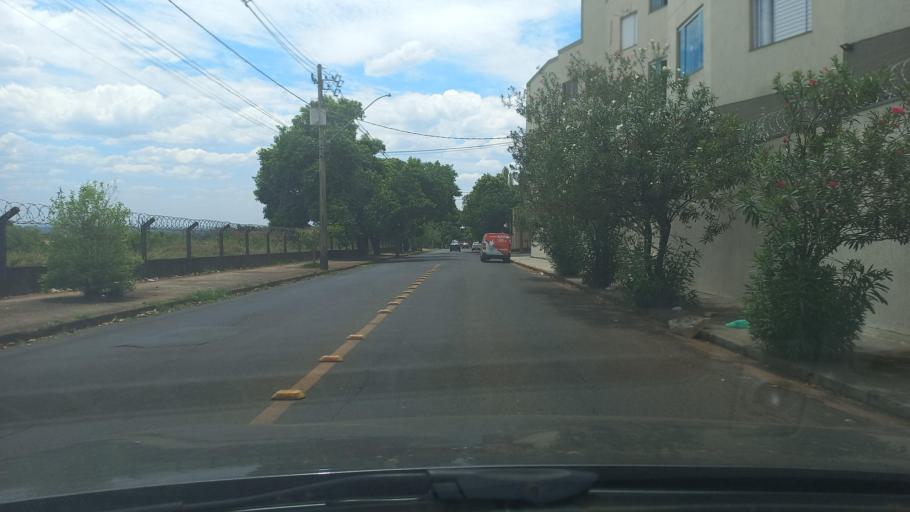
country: BR
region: Minas Gerais
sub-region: Uberaba
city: Uberaba
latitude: -19.7554
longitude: -47.9680
